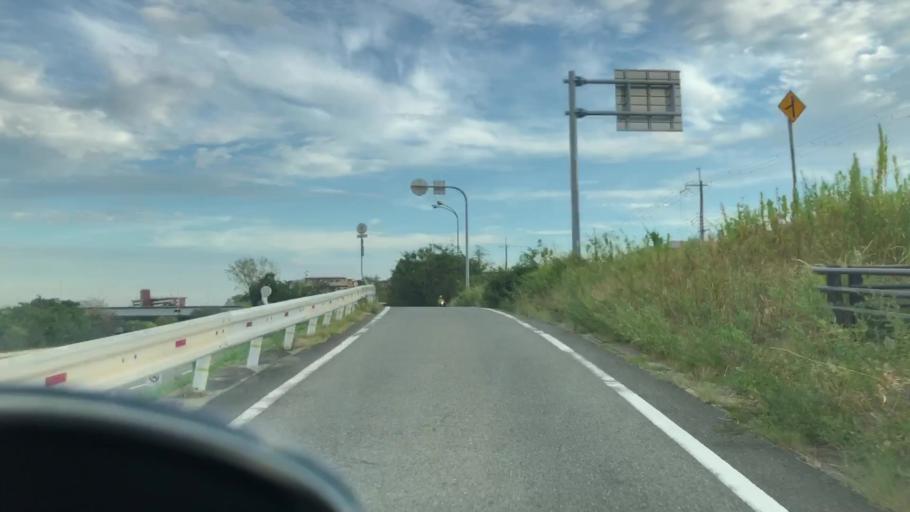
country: JP
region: Hyogo
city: Itami
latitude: 34.7470
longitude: 135.3749
